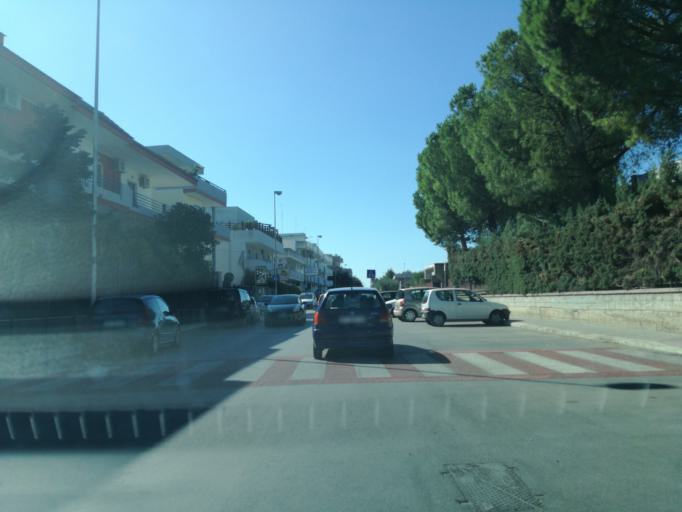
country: IT
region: Apulia
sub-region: Provincia di Bari
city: Capurso
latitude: 41.0503
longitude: 16.9155
